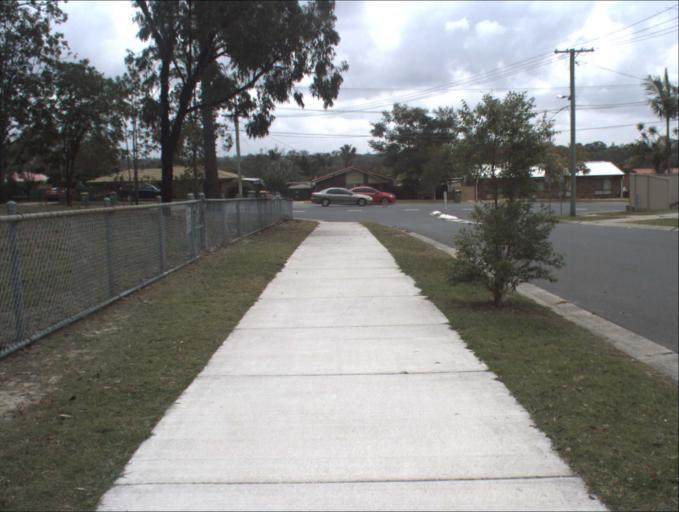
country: AU
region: Queensland
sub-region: Logan
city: Park Ridge South
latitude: -27.6766
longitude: 153.0509
